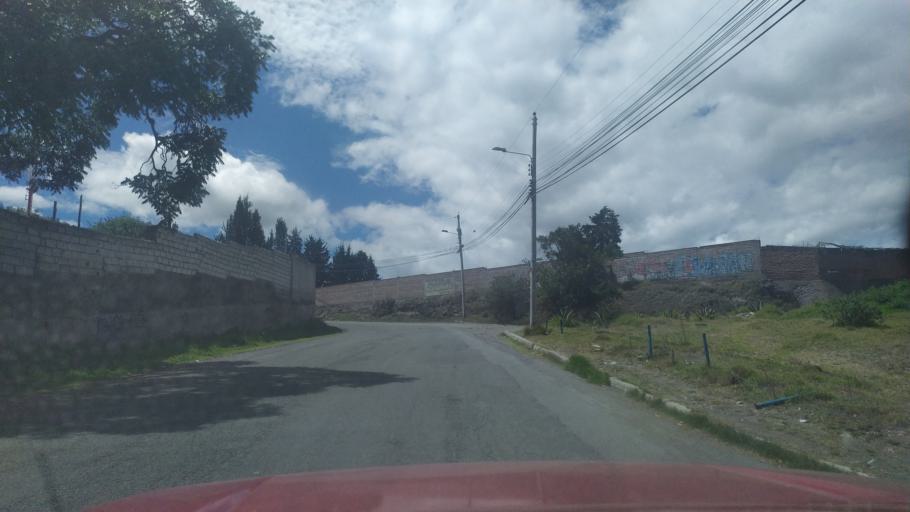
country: EC
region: Chimborazo
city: Riobamba
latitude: -1.6712
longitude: -78.6670
